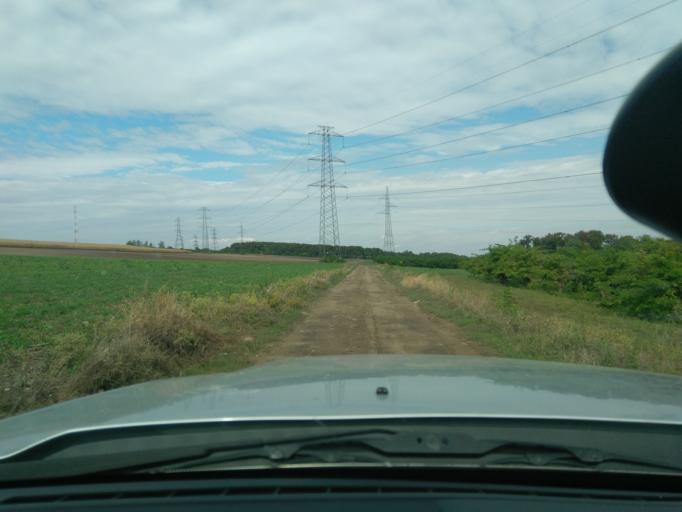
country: HU
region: Fejer
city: Val
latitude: 47.3736
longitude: 18.6954
